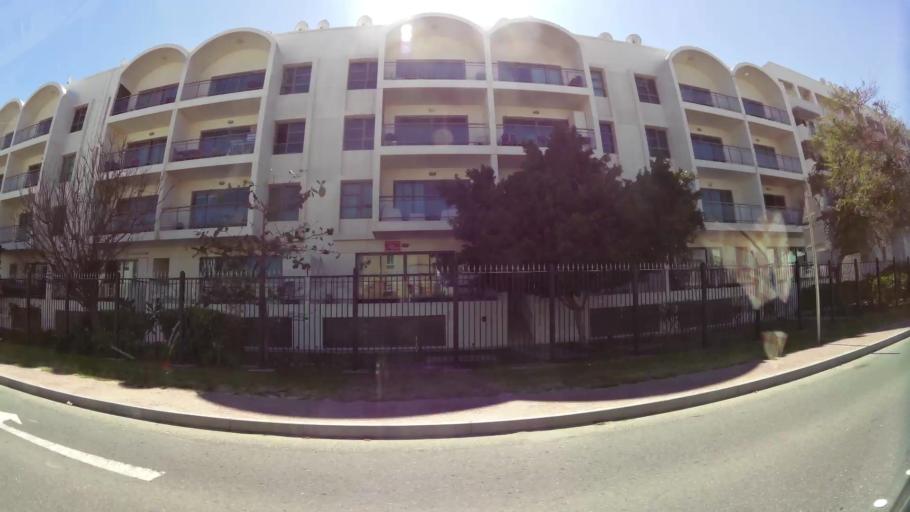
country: BH
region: Muharraq
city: Al Hadd
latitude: 26.2998
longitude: 50.6646
